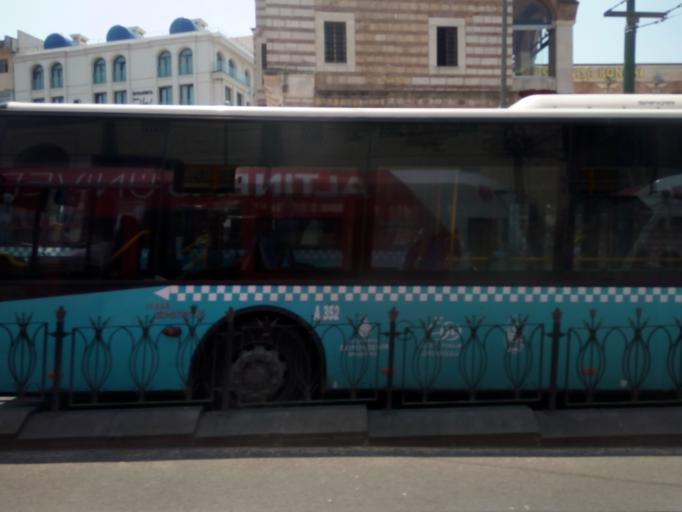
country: TR
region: Istanbul
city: Istanbul
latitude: 41.0096
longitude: 28.9619
